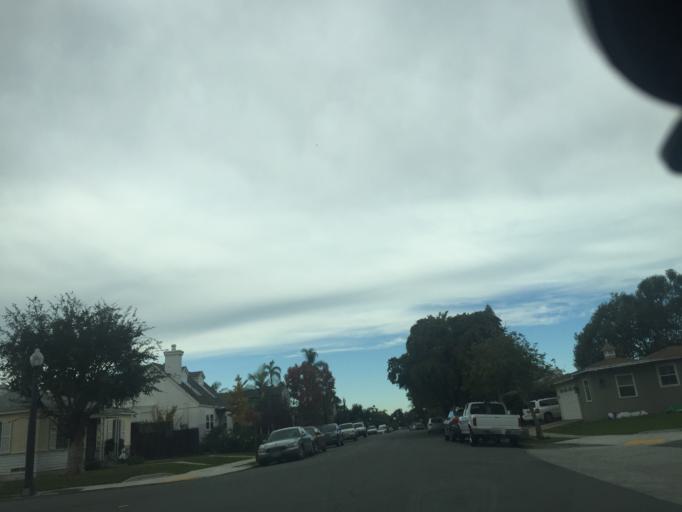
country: US
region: California
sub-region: San Diego County
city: Lemon Grove
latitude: 32.7629
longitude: -117.0848
